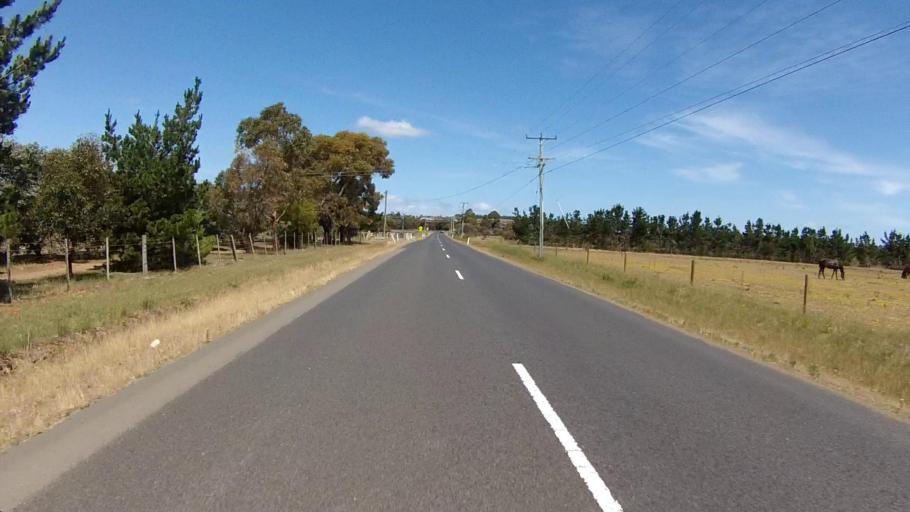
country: AU
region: Tasmania
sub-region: Sorell
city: Sorell
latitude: -42.7761
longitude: 147.5203
